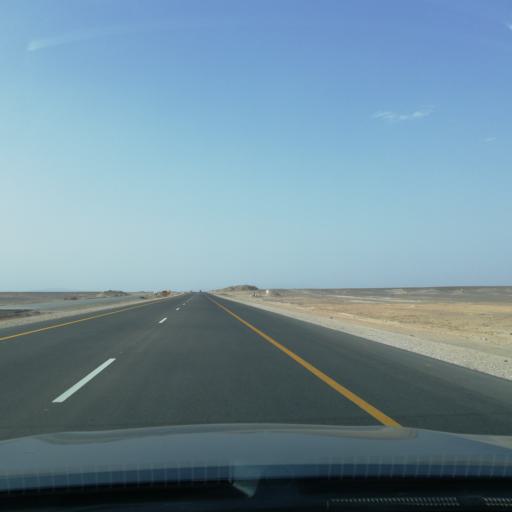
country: OM
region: Muhafazat ad Dakhiliyah
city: Adam
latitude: 22.1697
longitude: 57.5215
